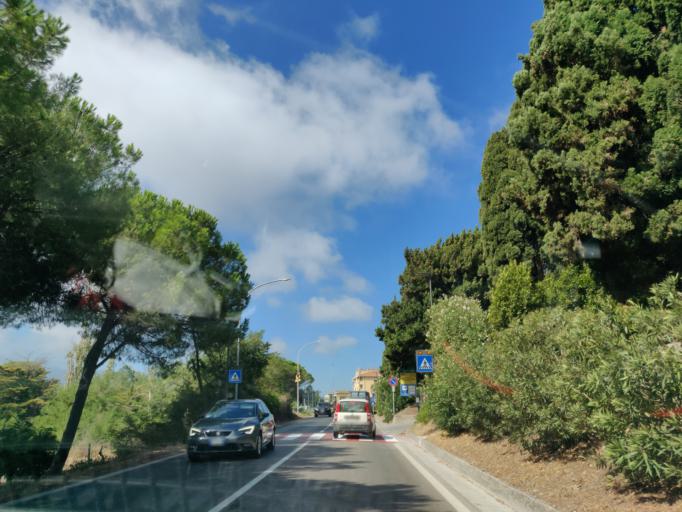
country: IT
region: Tuscany
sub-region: Provincia di Grosseto
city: Orbetello
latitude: 42.4448
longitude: 11.2339
